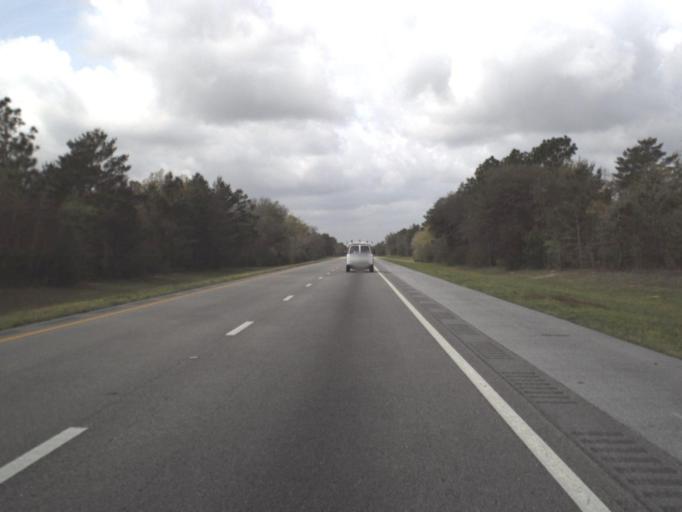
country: US
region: Florida
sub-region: Okaloosa County
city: Crestview
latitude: 30.7234
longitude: -86.4181
